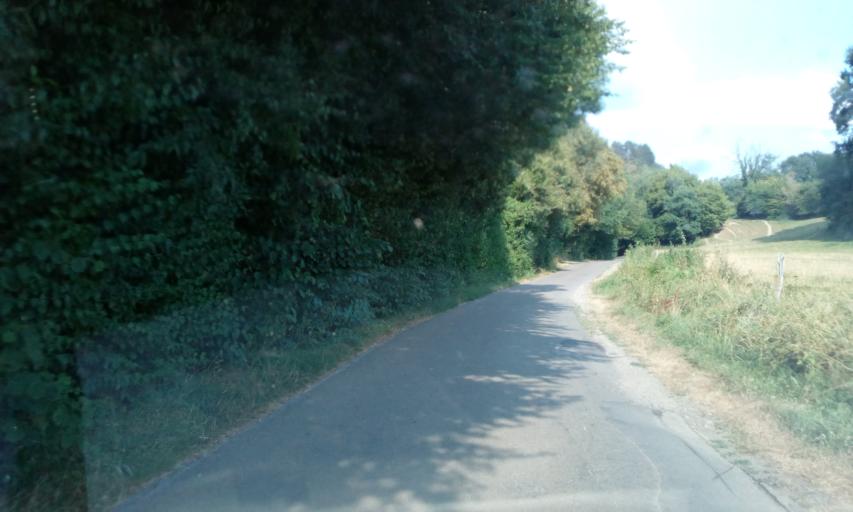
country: BE
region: Wallonia
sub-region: Province du Luxembourg
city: Tellin
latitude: 50.1103
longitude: 5.2017
